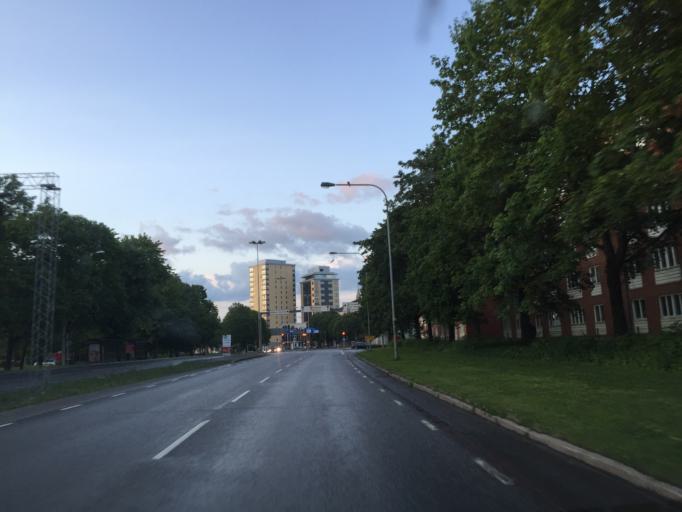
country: SE
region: OErebro
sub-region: Orebro Kommun
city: Orebro
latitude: 59.2686
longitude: 15.2021
